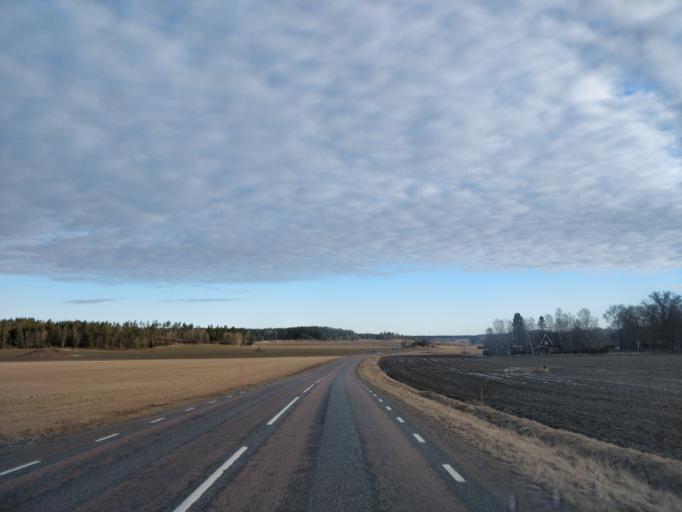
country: SE
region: Uppsala
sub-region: Enkopings Kommun
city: Enkoping
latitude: 59.7650
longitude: 17.0804
